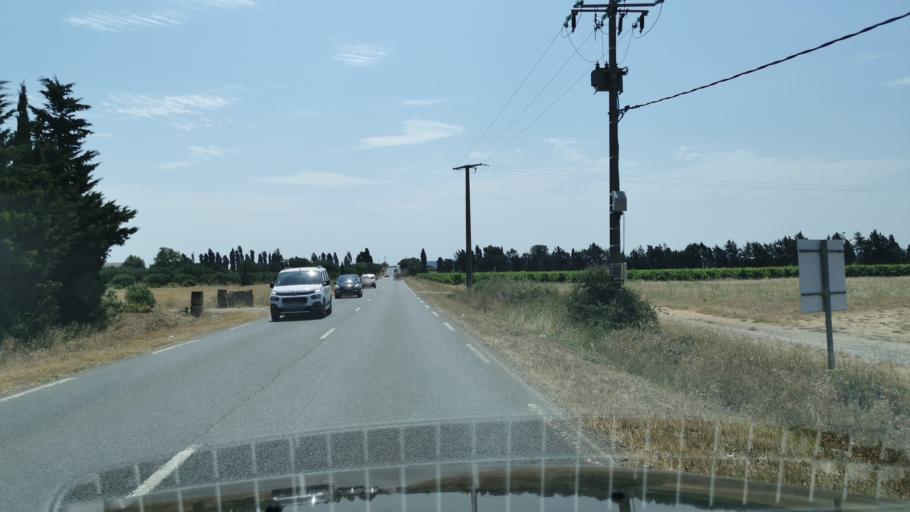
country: FR
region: Languedoc-Roussillon
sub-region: Departement de l'Aude
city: Ginestas
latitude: 43.2656
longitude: 2.9003
